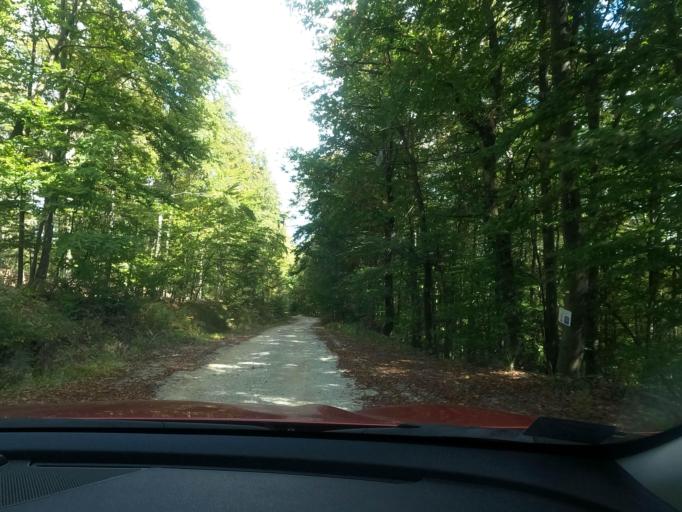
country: HR
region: Karlovacka
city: Vojnic
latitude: 45.3006
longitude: 15.7914
